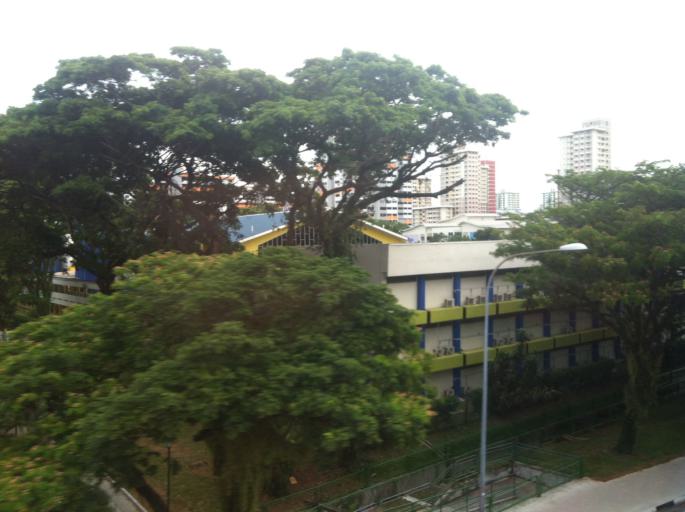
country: SG
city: Singapore
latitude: 1.3252
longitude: 103.9399
